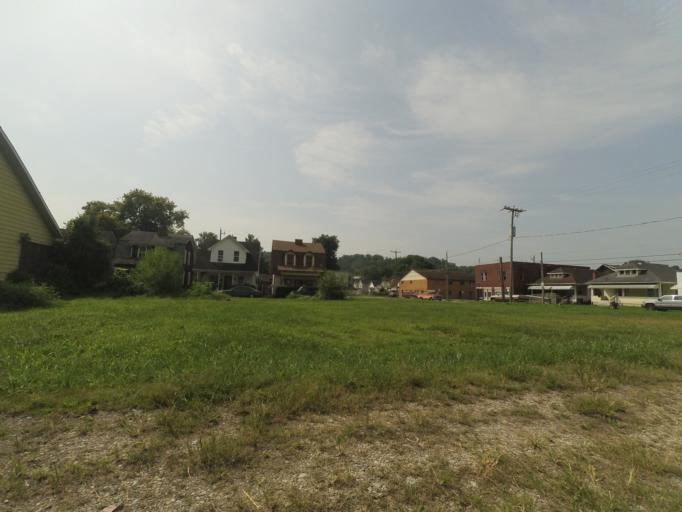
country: US
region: West Virginia
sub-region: Cabell County
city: Huntington
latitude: 38.4112
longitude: -82.4694
